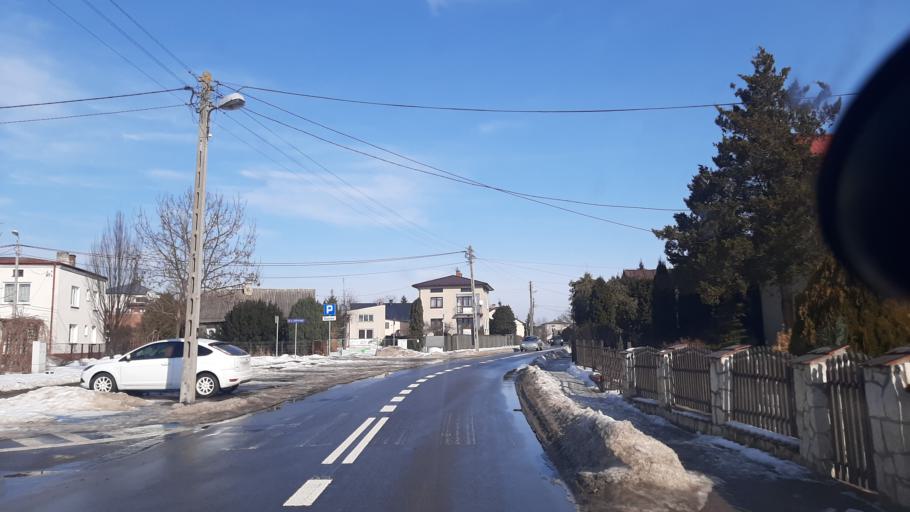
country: PL
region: Lublin Voivodeship
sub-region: Powiat pulawski
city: Kurow
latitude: 51.3901
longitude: 22.1884
